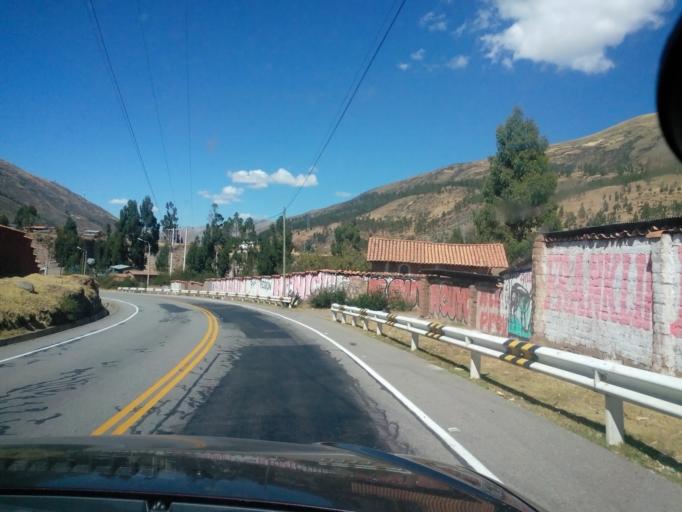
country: PE
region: Cusco
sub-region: Provincia de Canchis
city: Checacupe
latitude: -14.0236
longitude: -71.4577
